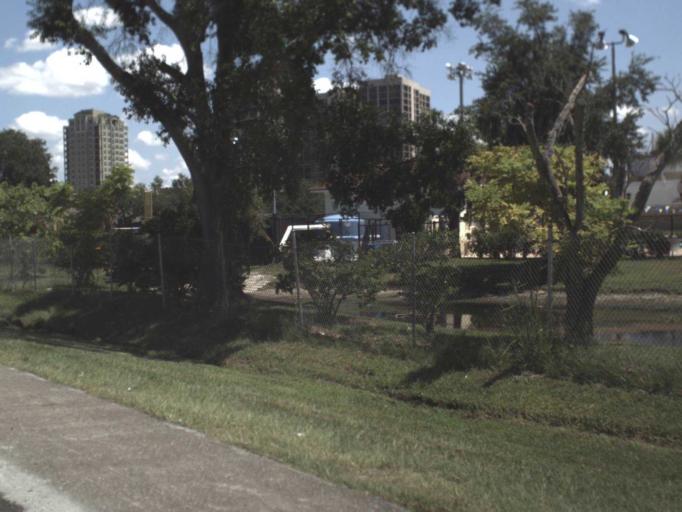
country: US
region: Florida
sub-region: Hillsborough County
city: Tampa
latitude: 27.9146
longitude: -82.4960
